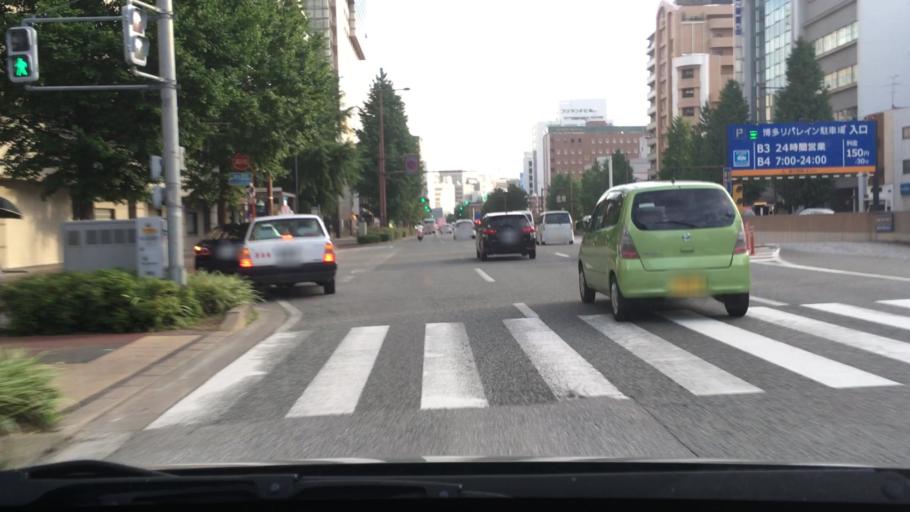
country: JP
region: Fukuoka
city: Fukuoka-shi
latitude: 33.5971
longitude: 130.4060
